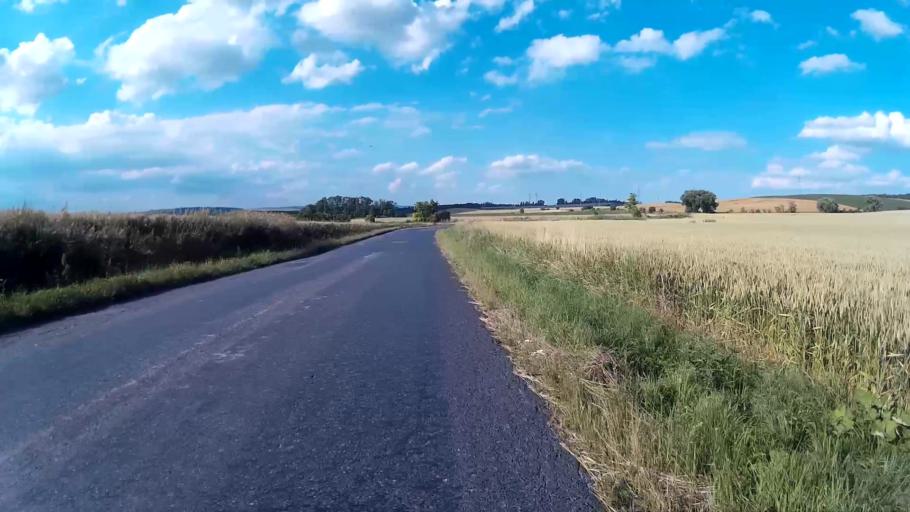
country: CZ
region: South Moravian
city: Tesany
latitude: 49.0594
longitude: 16.7811
